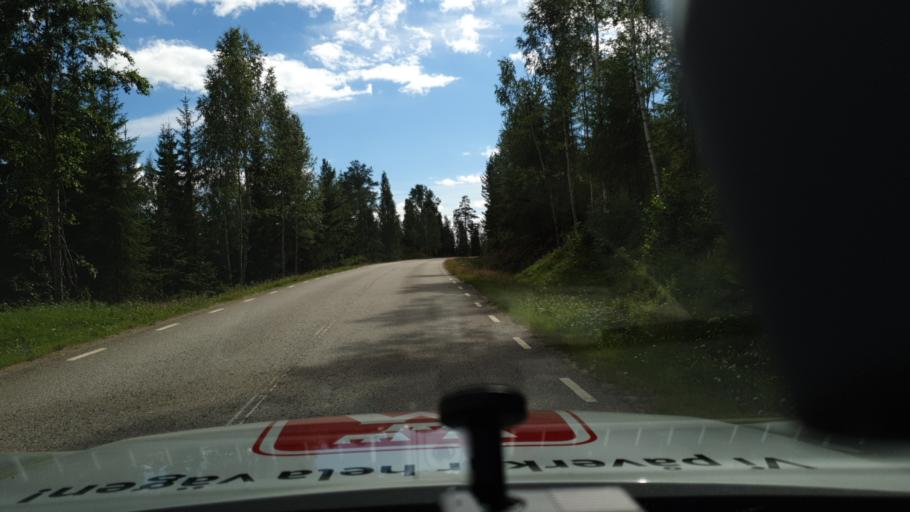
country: NO
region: Hedmark
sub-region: Trysil
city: Innbygda
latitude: 61.0339
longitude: 12.5852
